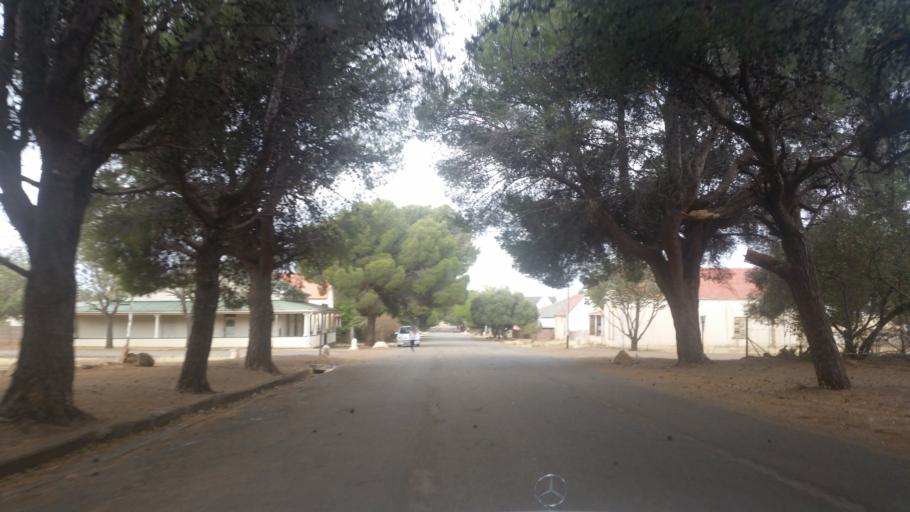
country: ZA
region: Orange Free State
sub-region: Xhariep District Municipality
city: Trompsburg
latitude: -30.4962
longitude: 25.9706
